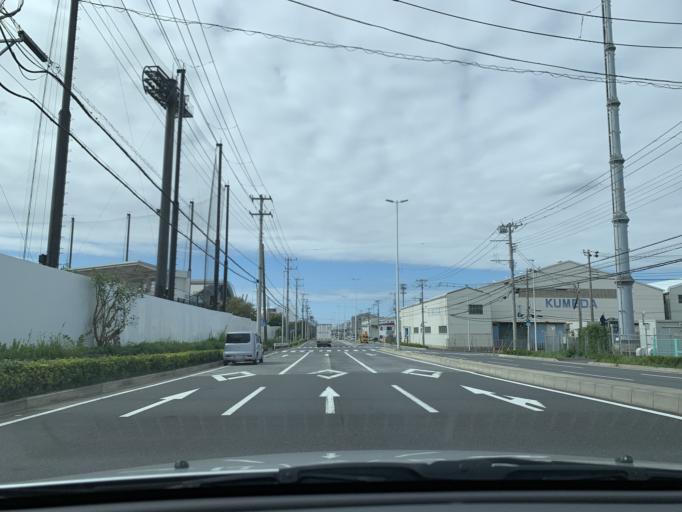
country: JP
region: Tokyo
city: Urayasu
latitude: 35.6290
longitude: 139.8948
